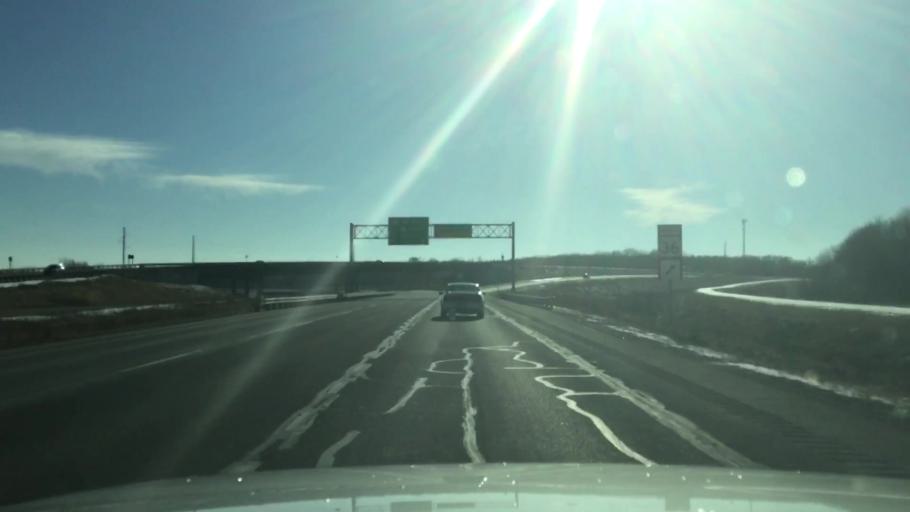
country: US
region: Wisconsin
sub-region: Racine County
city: Rochester
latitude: 42.7193
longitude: -88.2251
